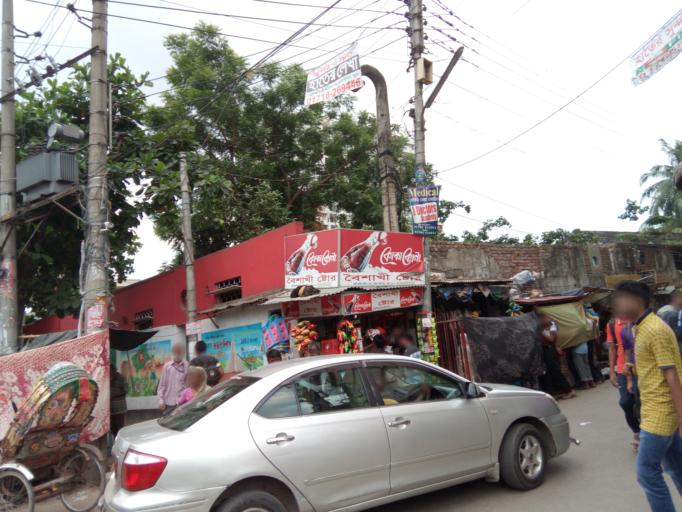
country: BD
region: Dhaka
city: Paltan
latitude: 23.7321
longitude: 90.4237
